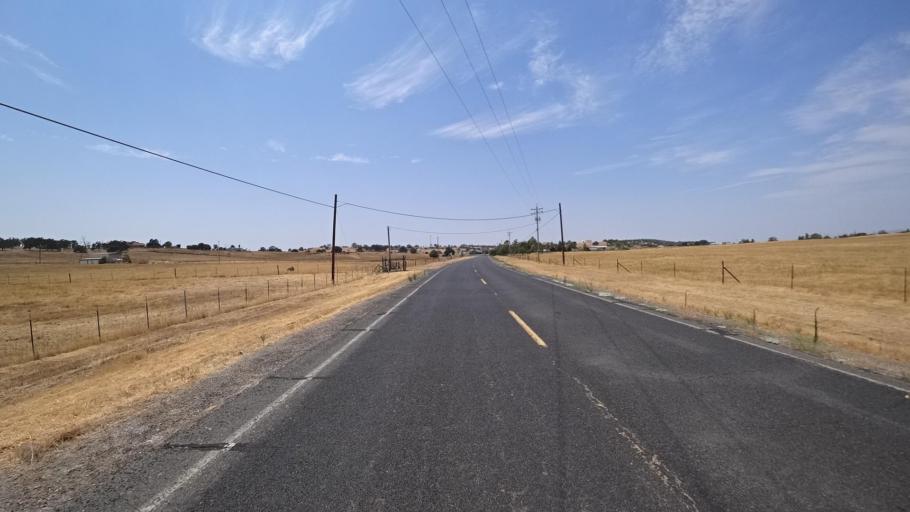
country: US
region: California
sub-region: Tuolumne County
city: Jamestown
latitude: 37.6452
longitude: -120.3201
